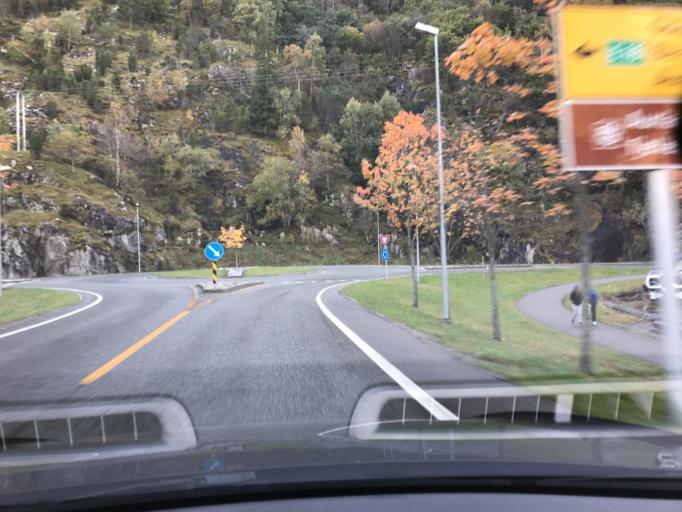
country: NO
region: Sogn og Fjordane
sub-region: Laerdal
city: Laerdalsoyri
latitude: 61.0988
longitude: 7.4713
